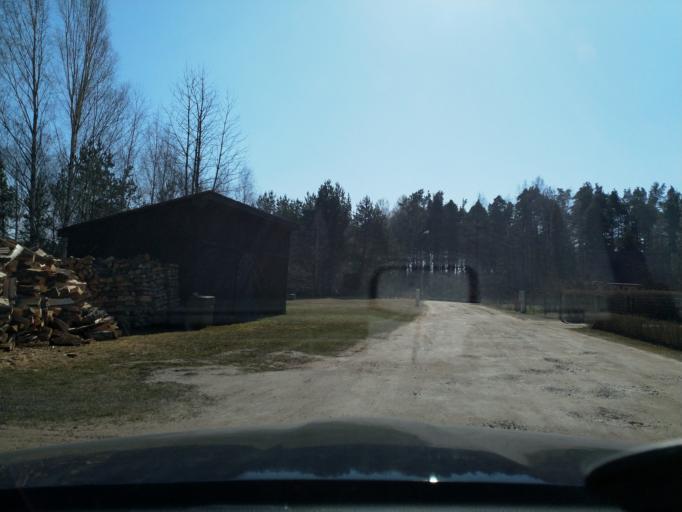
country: LV
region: Kuldigas Rajons
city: Kuldiga
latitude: 56.9642
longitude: 21.9315
